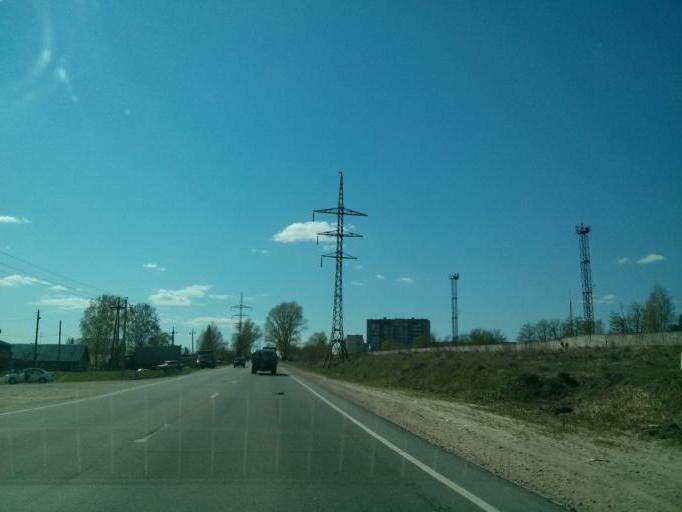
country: RU
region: Nizjnij Novgorod
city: Taremskoye
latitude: 55.9353
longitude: 43.0642
